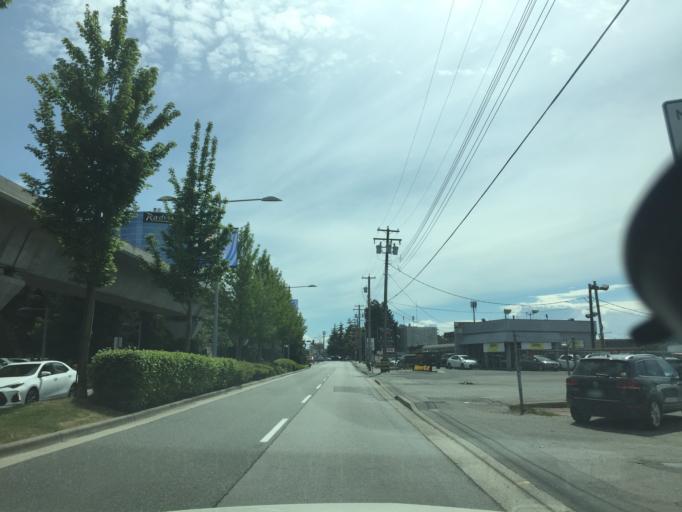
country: CA
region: British Columbia
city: Richmond
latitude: 49.1865
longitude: -123.1349
